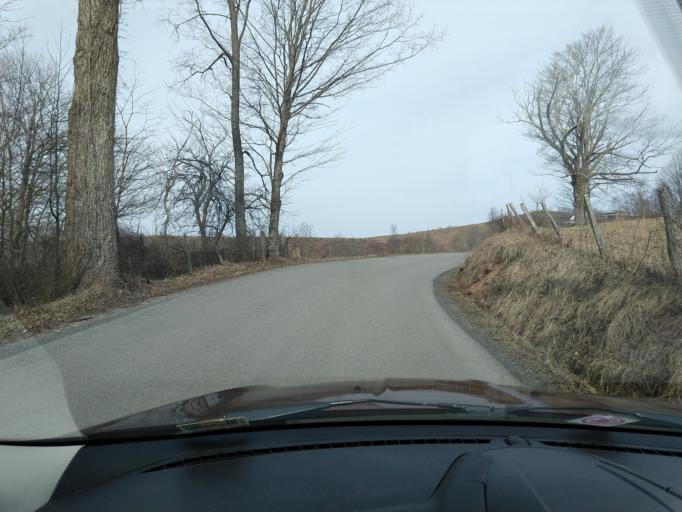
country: US
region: West Virginia
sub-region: Tucker County
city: Parsons
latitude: 39.0084
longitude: -79.5098
